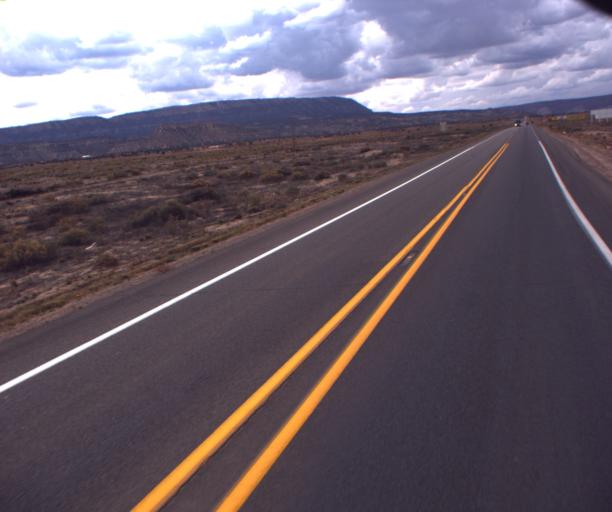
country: US
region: Arizona
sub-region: Navajo County
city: Kayenta
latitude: 36.7060
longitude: -110.2590
